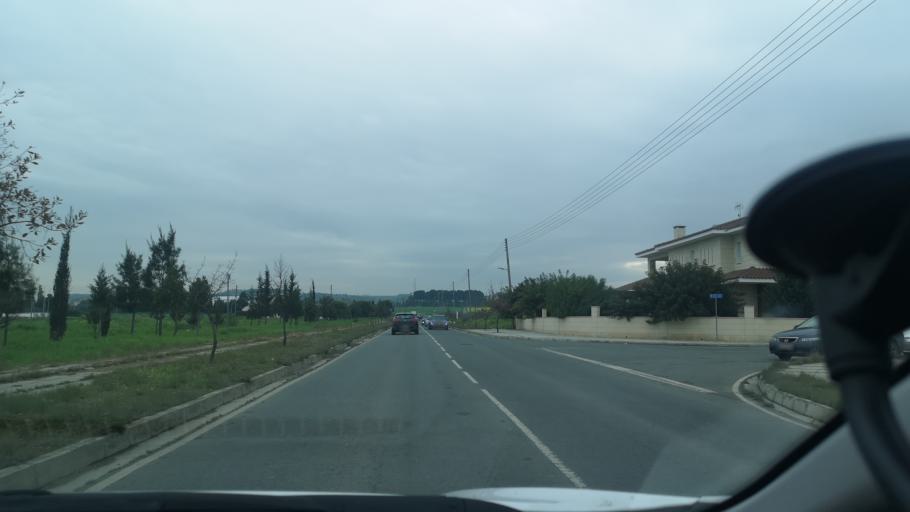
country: CY
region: Lefkosia
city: Tseri
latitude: 35.1045
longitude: 33.3493
